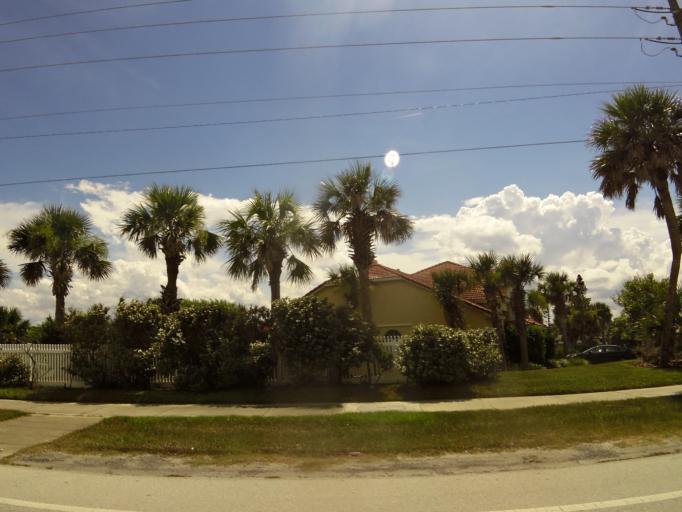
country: US
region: Florida
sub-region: Volusia County
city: Ormond Beach
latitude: 29.3126
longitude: -81.0502
